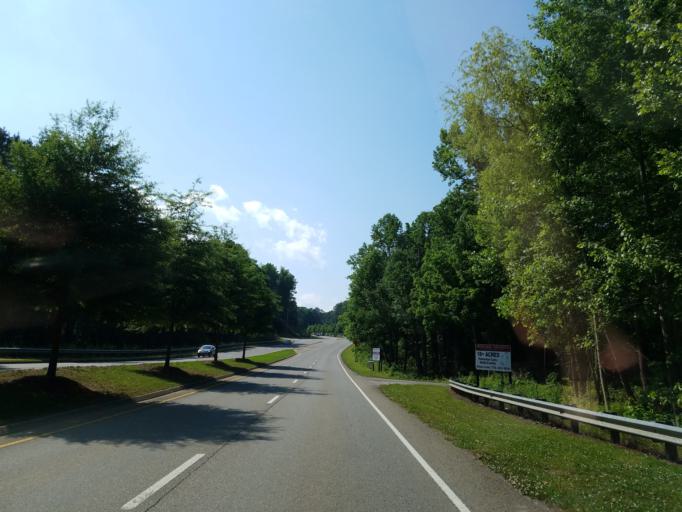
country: US
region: Georgia
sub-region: Cherokee County
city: Holly Springs
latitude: 34.1513
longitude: -84.5201
